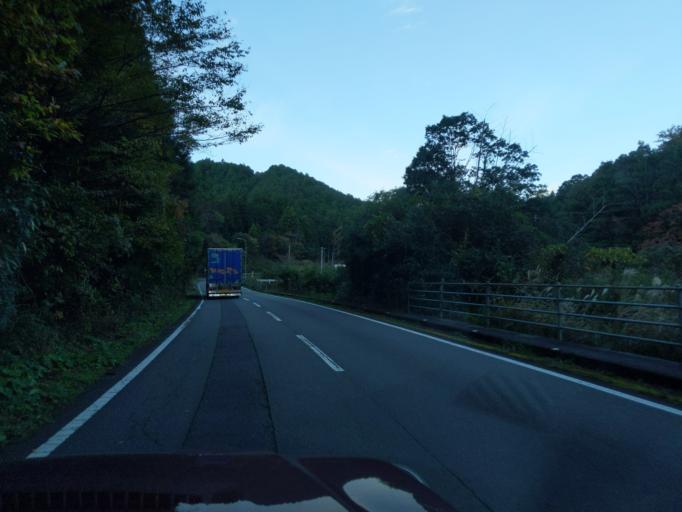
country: JP
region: Tokushima
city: Anan
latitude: 33.7097
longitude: 134.4702
